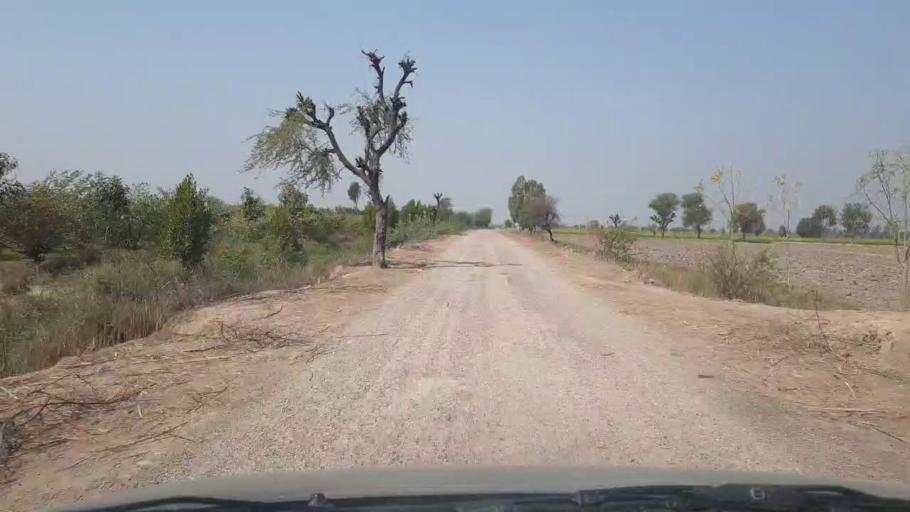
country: PK
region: Sindh
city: Mirwah Gorchani
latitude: 25.3437
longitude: 69.1434
